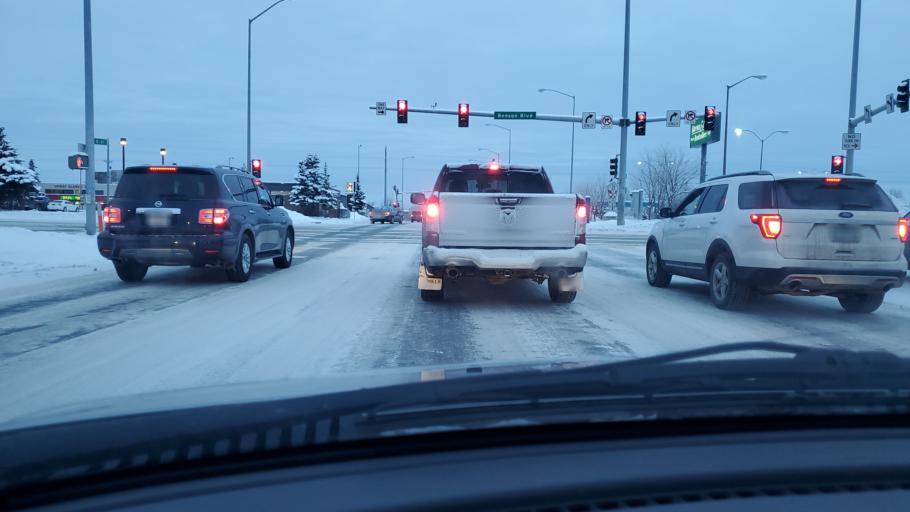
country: US
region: Alaska
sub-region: Anchorage Municipality
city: Anchorage
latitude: 61.1939
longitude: -149.8831
